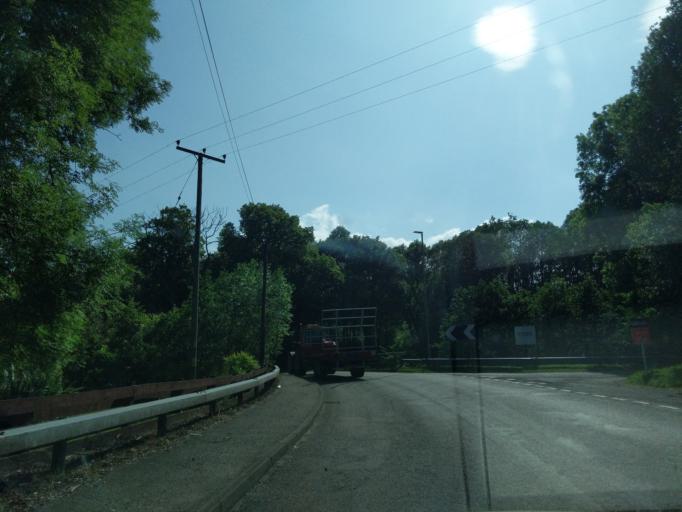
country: GB
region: Scotland
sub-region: Moray
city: Rothes
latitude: 57.5350
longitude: -3.2076
